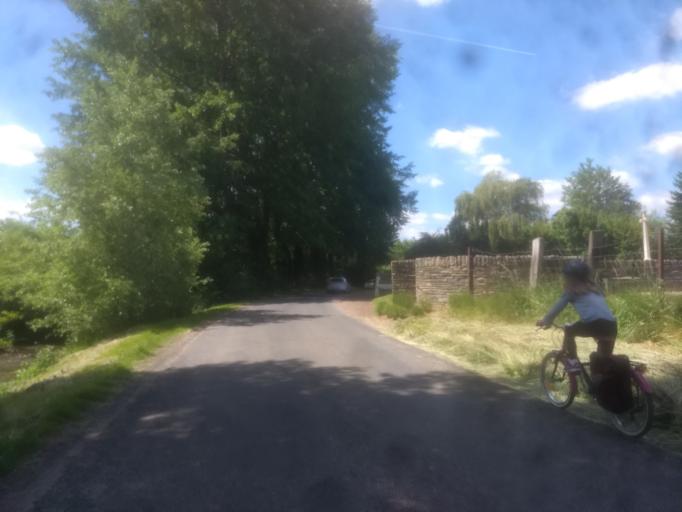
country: FR
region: Nord-Pas-de-Calais
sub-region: Departement du Pas-de-Calais
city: Riviere
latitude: 50.2403
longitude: 2.7051
